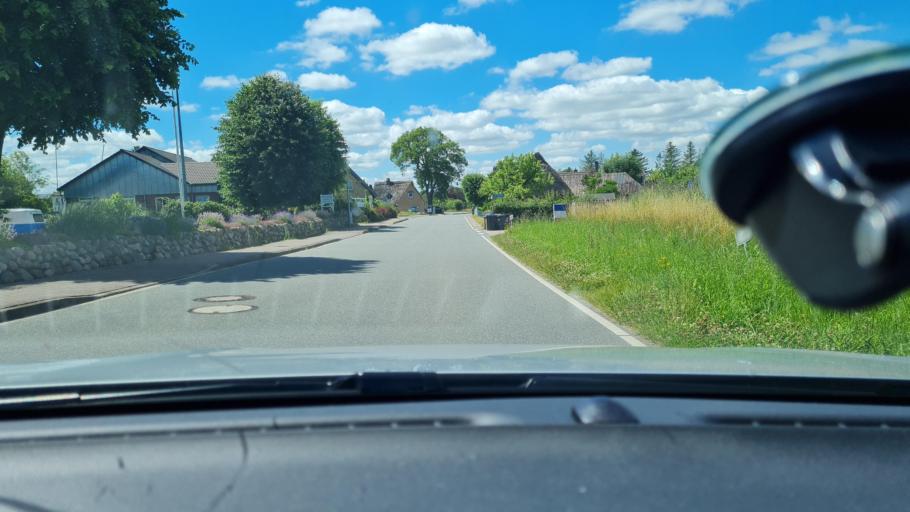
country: DE
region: Schleswig-Holstein
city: Winnemark
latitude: 54.6176
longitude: 9.9263
